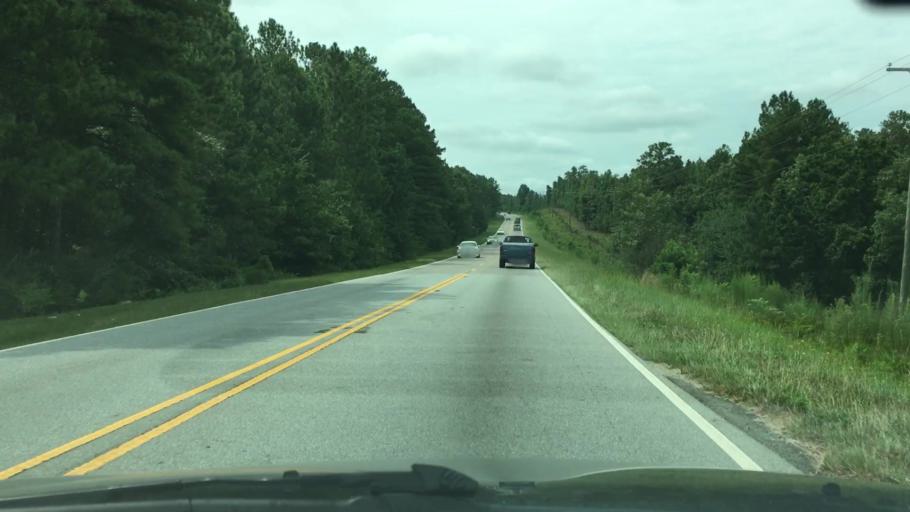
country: US
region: South Carolina
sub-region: Aiken County
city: Warrenville
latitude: 33.5418
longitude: -81.7756
